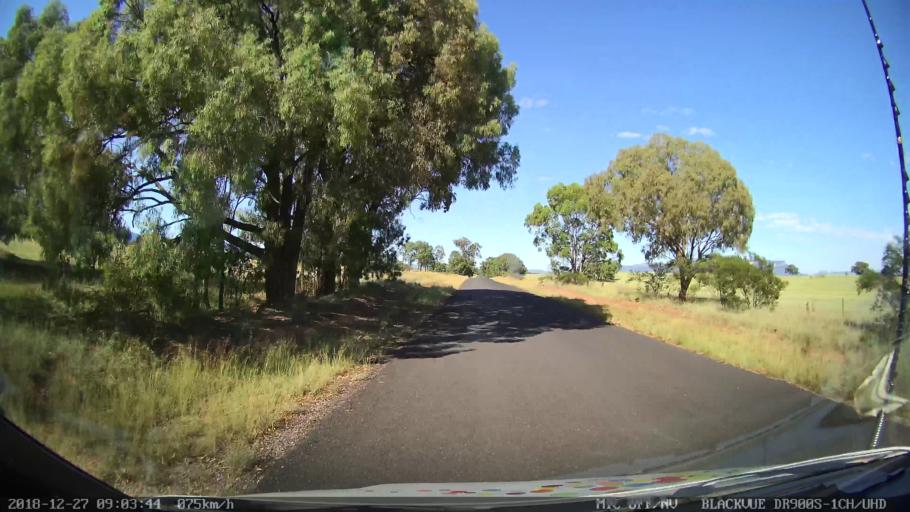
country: AU
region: New South Wales
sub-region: Lithgow
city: Portland
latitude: -33.1065
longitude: 150.1984
